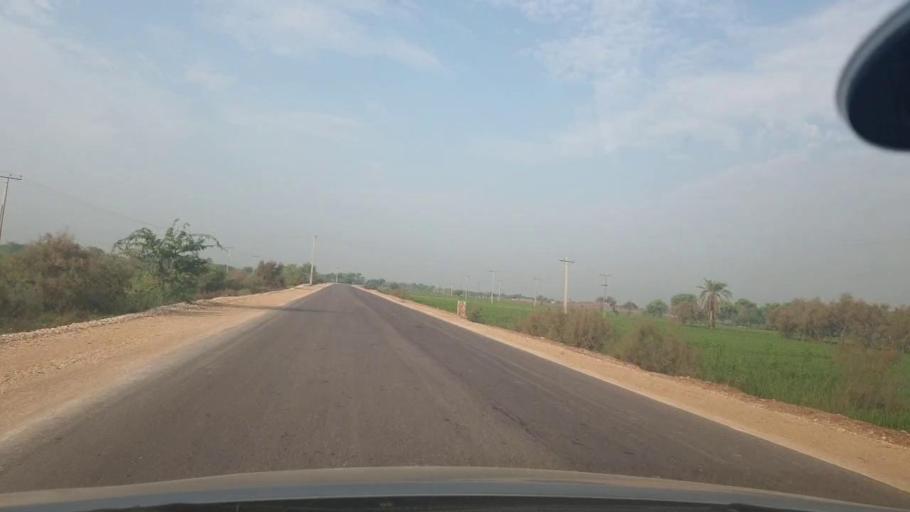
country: PK
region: Sindh
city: Jacobabad
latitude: 28.2495
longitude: 68.4032
